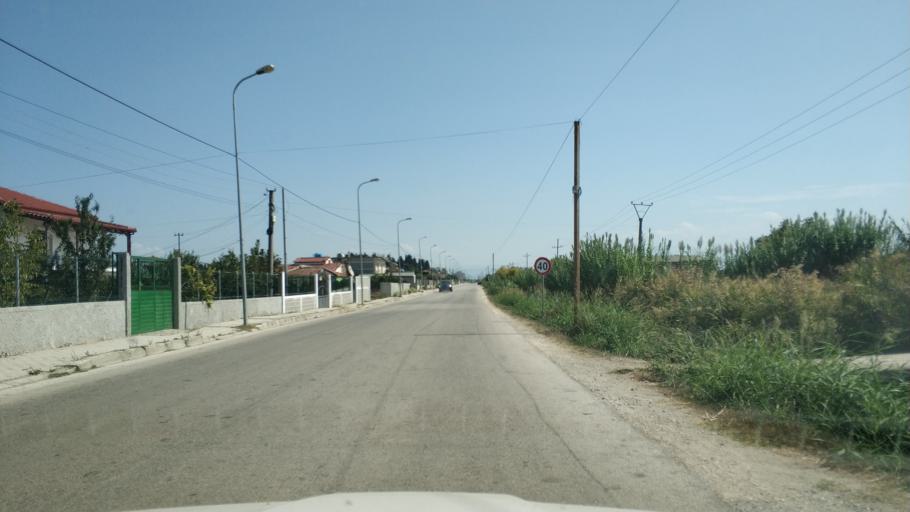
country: AL
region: Fier
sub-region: Rrethi i Lushnjes
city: Gradishte
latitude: 40.8848
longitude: 19.5716
